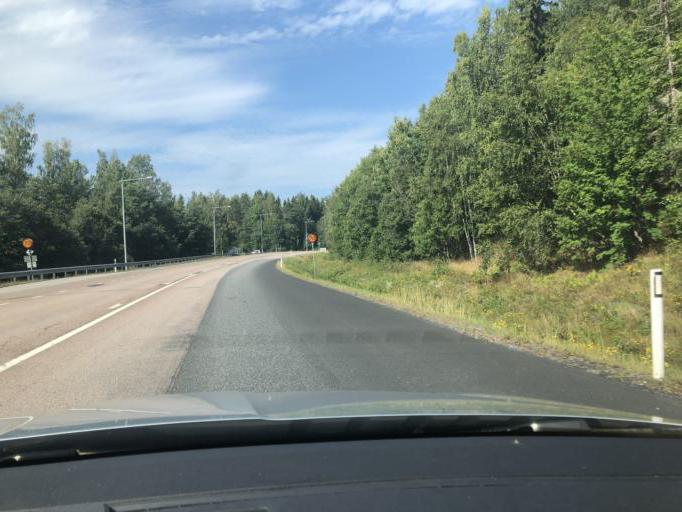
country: SE
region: Vaesternorrland
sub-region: Kramfors Kommun
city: Kramfors
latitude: 62.7981
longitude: 17.8759
